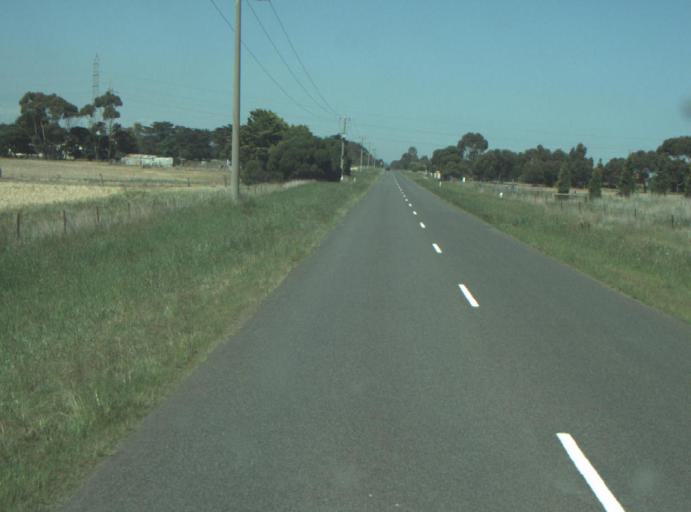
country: AU
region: Victoria
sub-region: Greater Geelong
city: Lara
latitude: -38.0187
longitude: 144.3602
